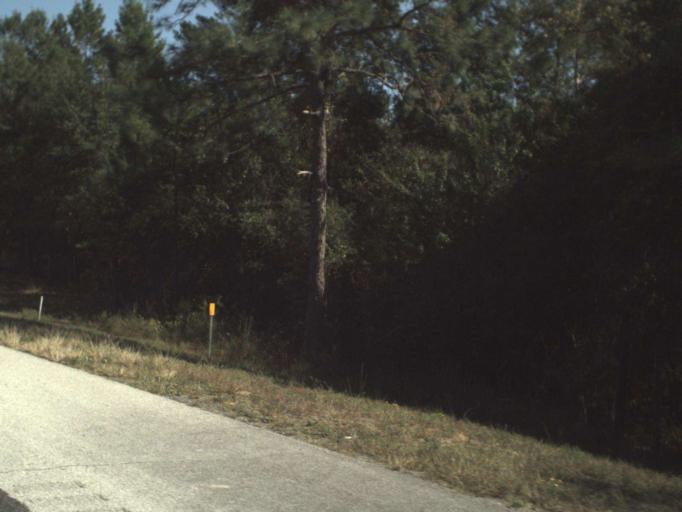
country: US
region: Florida
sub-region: Walton County
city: DeFuniak Springs
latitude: 30.7329
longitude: -86.3361
